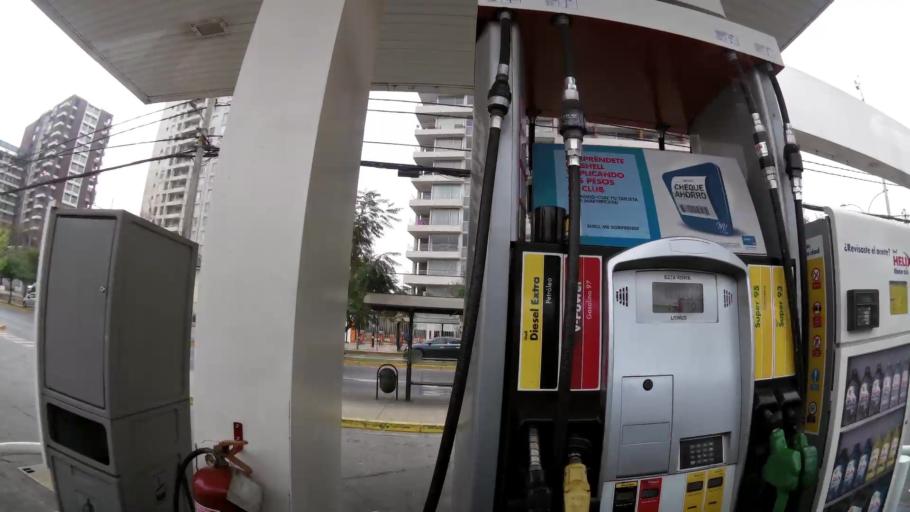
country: CL
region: Santiago Metropolitan
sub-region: Provincia de Santiago
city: Villa Presidente Frei, Nunoa, Santiago, Chile
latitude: -33.4557
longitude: -70.5864
